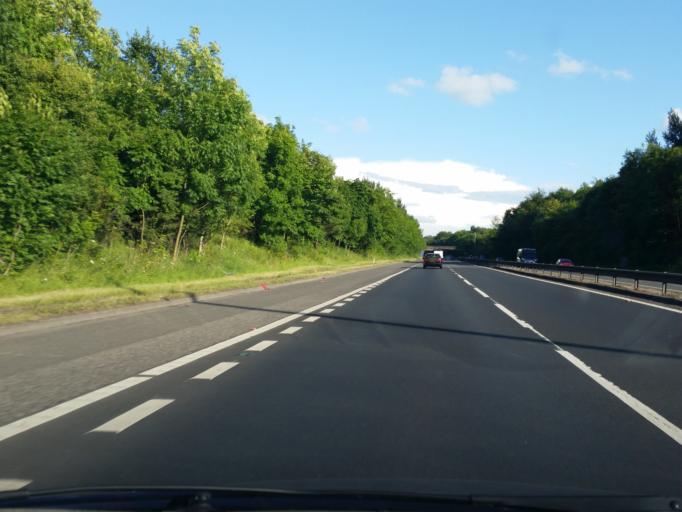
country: GB
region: Scotland
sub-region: South Lanarkshire
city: Hamilton
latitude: 55.7761
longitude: -4.0151
